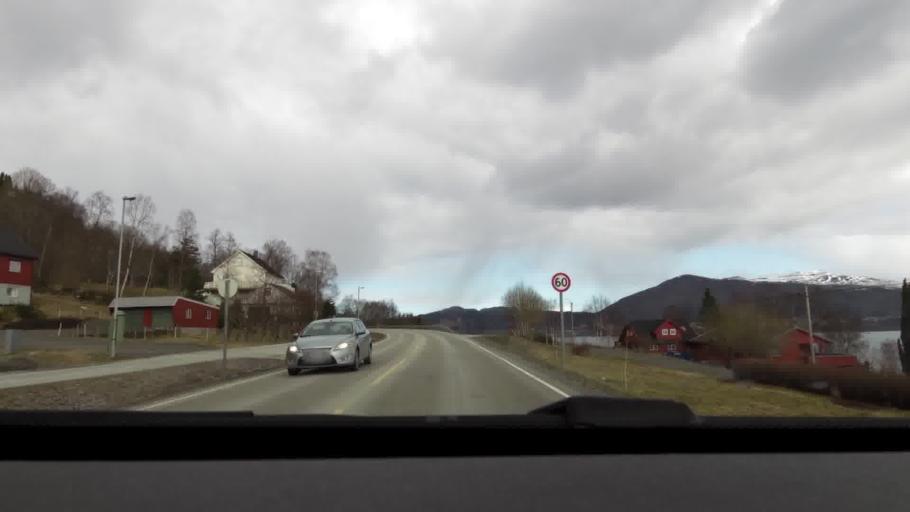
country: NO
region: More og Romsdal
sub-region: Eide
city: Eide
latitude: 62.9263
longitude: 7.4472
